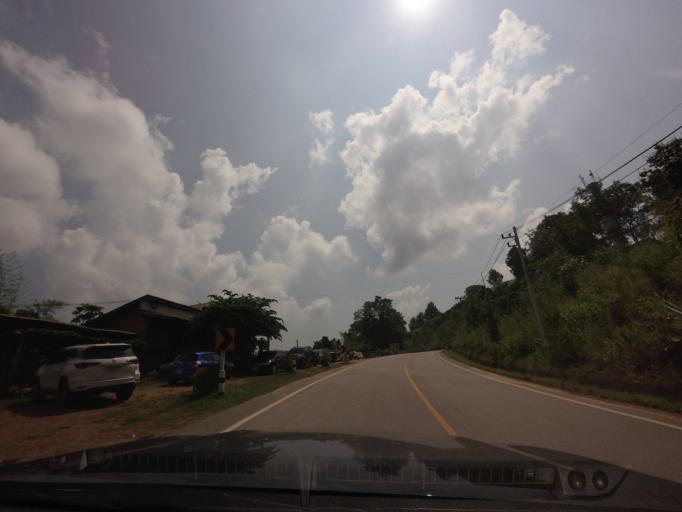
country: TH
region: Nan
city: Santi Suk
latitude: 18.9151
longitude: 100.8812
